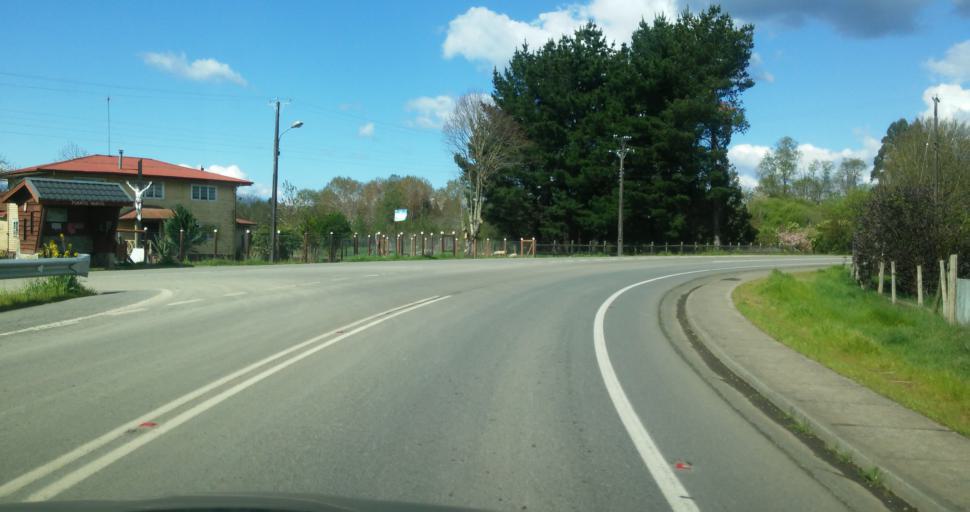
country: CL
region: Los Rios
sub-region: Provincia del Ranco
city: Rio Bueno
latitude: -40.2390
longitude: -72.5932
